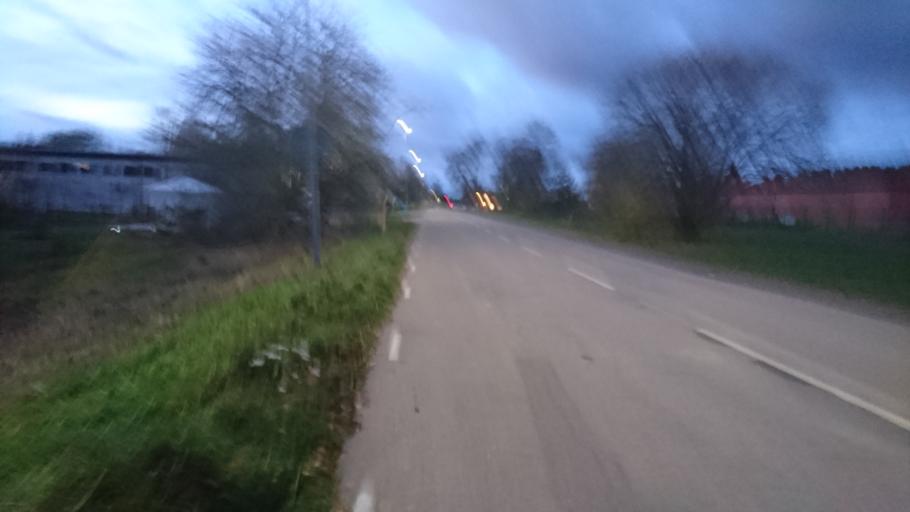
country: SE
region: Vaestmanland
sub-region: Sala Kommun
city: Sala
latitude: 59.8080
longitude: 16.6399
